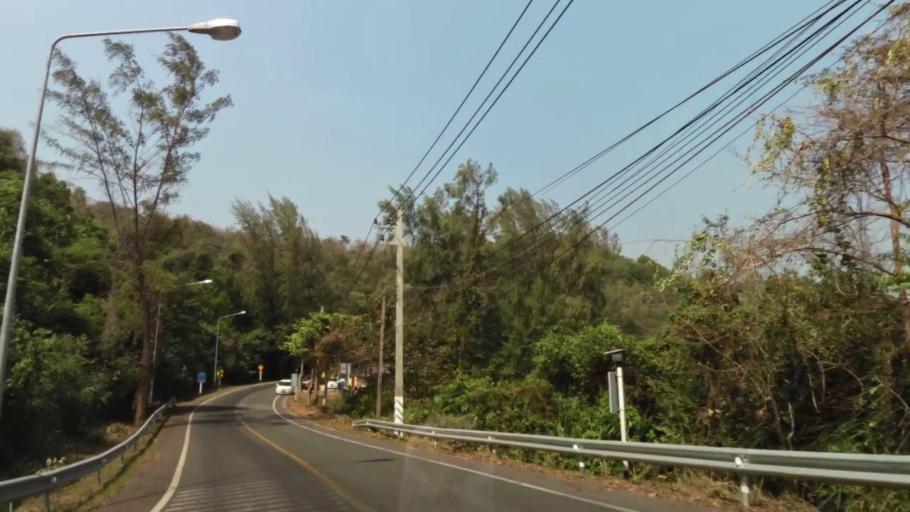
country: TH
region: Chanthaburi
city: Tha Mai
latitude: 12.5244
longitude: 101.9484
